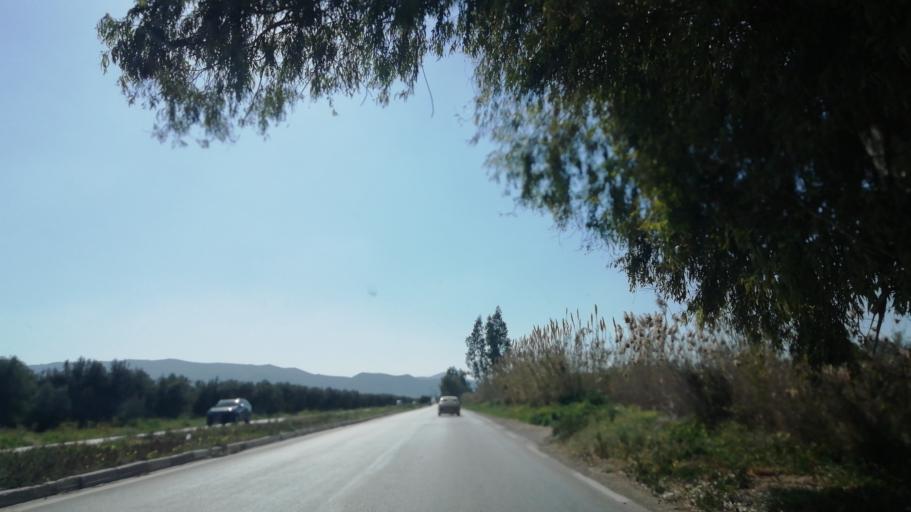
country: DZ
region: Mascara
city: Sig
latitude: 35.5509
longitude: -0.2062
